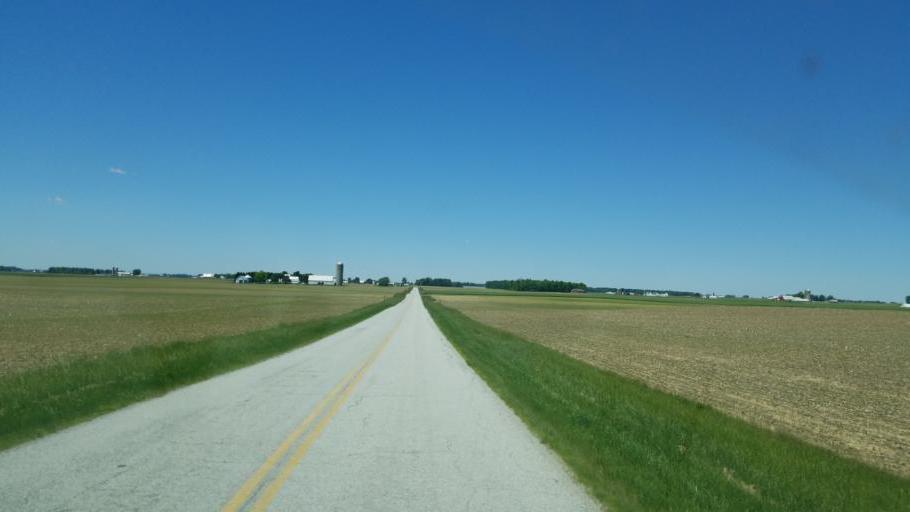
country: US
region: Ohio
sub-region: Auglaize County
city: Minster
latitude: 40.3856
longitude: -84.4412
